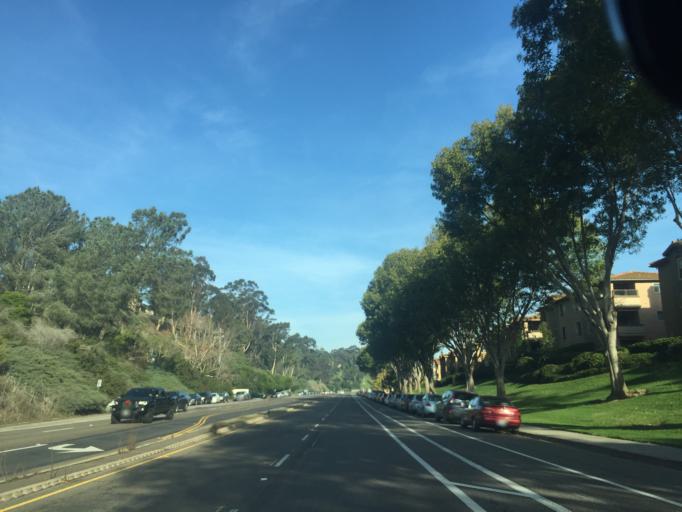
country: US
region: California
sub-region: San Diego County
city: La Jolla
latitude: 32.8647
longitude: -117.2363
